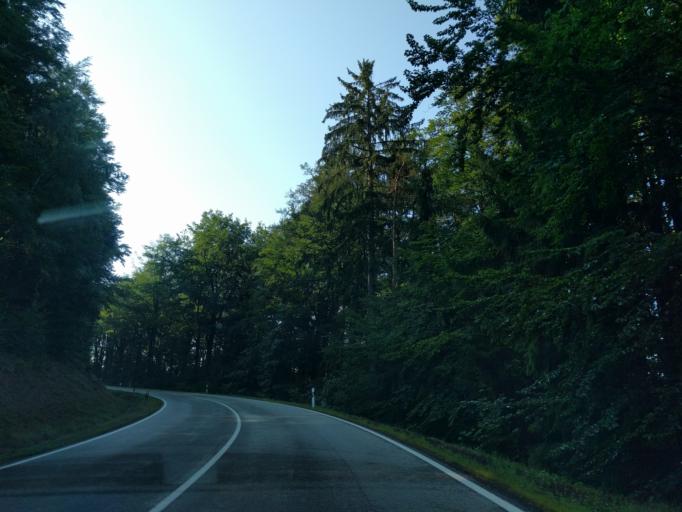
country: DE
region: Bavaria
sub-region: Lower Bavaria
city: Grafenau
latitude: 48.8544
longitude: 13.4102
